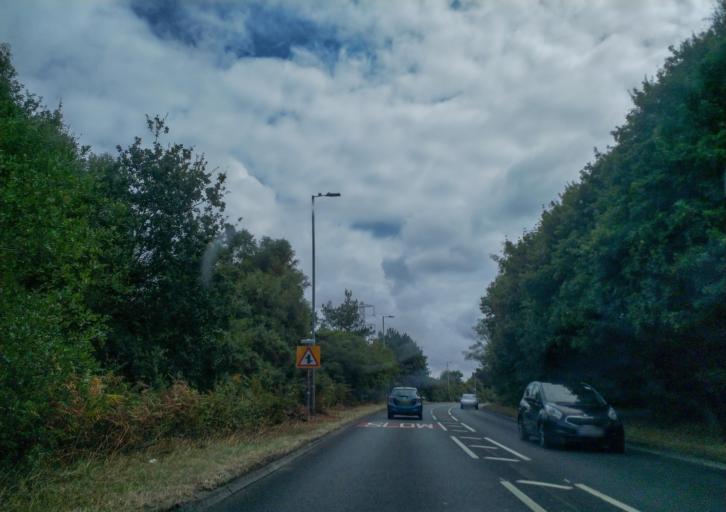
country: GB
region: England
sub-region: Bracknell Forest
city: Sandhurst
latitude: 51.3585
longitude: -0.7830
